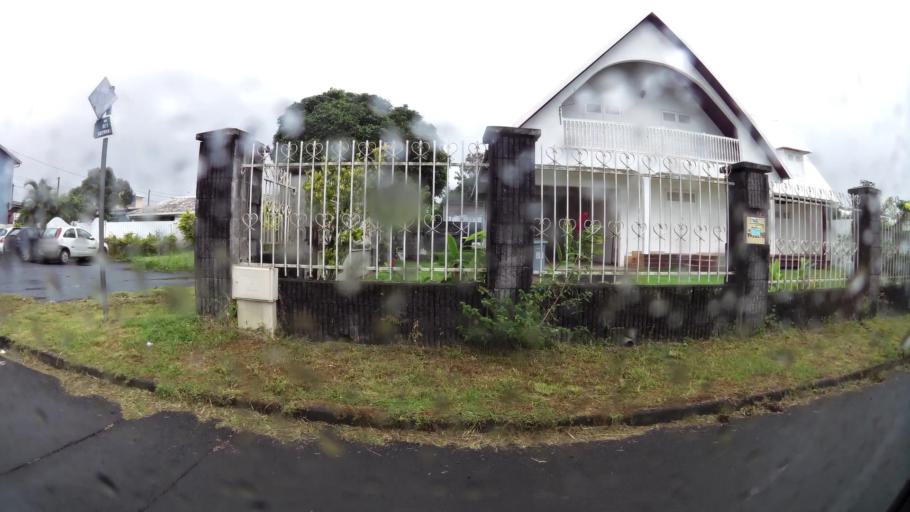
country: RE
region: Reunion
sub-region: Reunion
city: Saint-Andre
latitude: -20.9563
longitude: 55.6558
